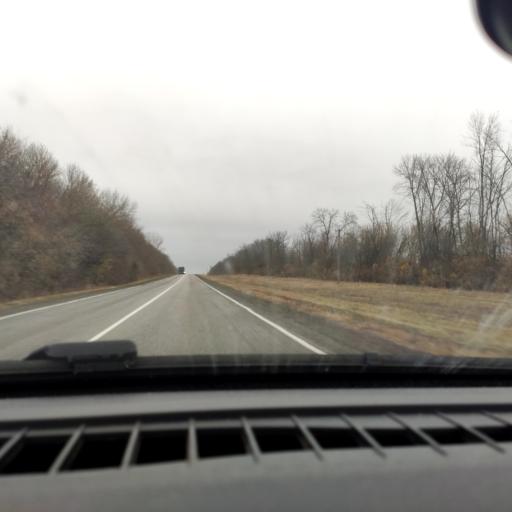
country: RU
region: Voronezj
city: Uryv-Pokrovka
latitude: 51.1066
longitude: 39.0215
